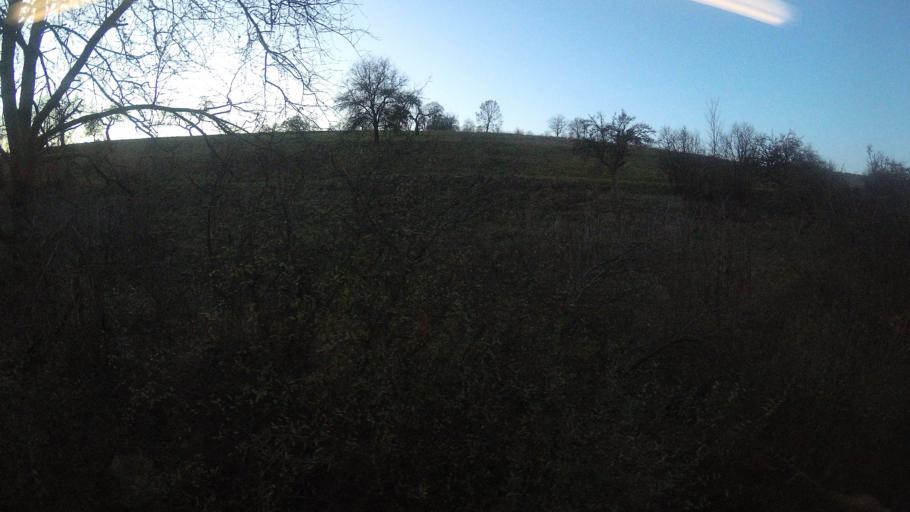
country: DE
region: Rheinland-Pfalz
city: Herchweiler
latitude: 49.4957
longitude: 7.2626
